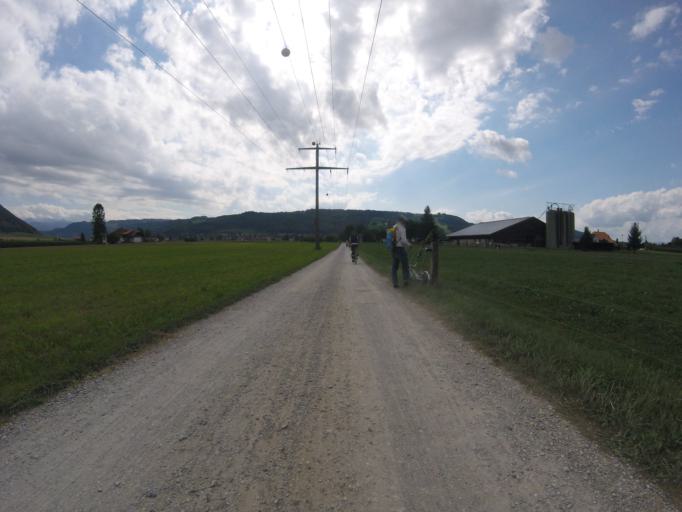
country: CH
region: Bern
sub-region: Bern-Mittelland District
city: Belp
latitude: 46.9014
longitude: 7.5160
